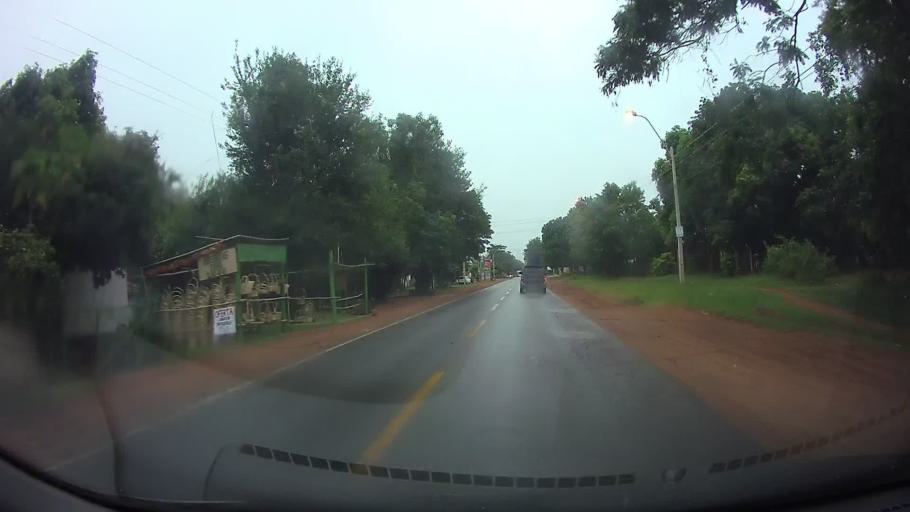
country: PY
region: Central
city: Ita
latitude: -25.4975
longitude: -57.3579
